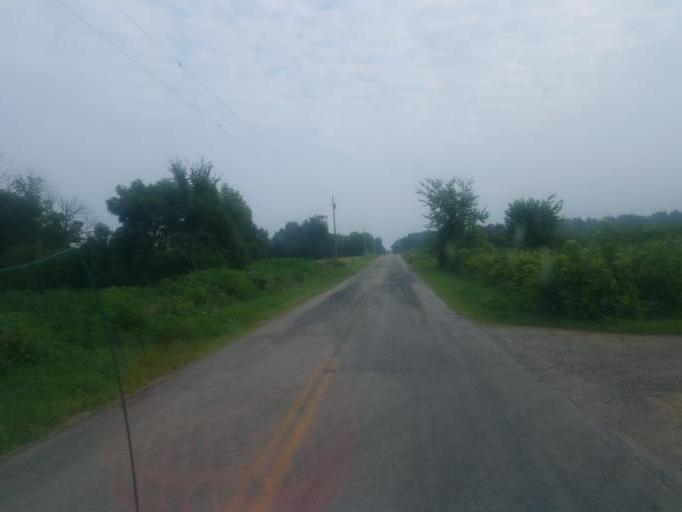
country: US
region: Ohio
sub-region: Morrow County
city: Cardington
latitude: 40.5613
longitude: -82.9766
